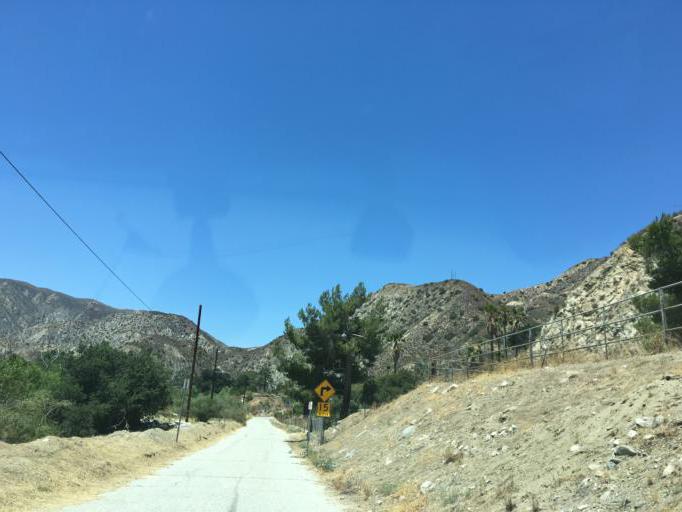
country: US
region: California
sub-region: Los Angeles County
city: La Crescenta-Montrose
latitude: 34.3014
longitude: -118.2540
